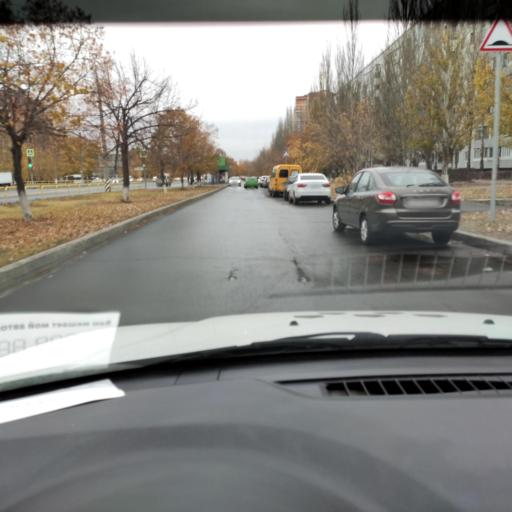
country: RU
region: Samara
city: Tol'yatti
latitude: 53.5106
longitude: 49.2933
